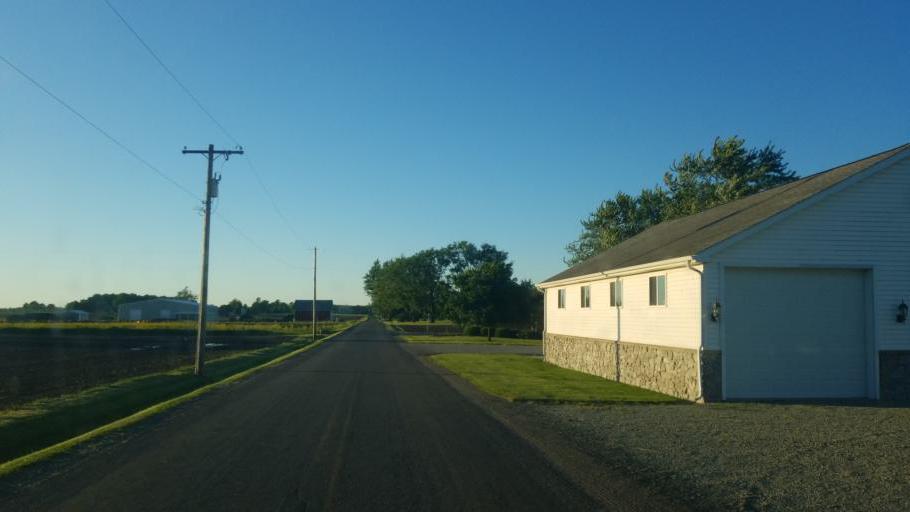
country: US
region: Indiana
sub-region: Elkhart County
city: Nappanee
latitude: 41.4563
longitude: -86.0497
